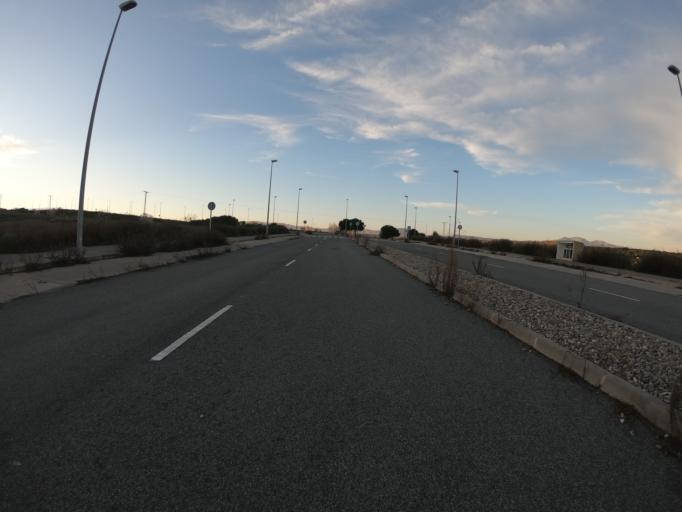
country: ES
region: Basque Country
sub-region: Provincia de Alava
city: Oyon
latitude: 42.4853
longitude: -2.4155
